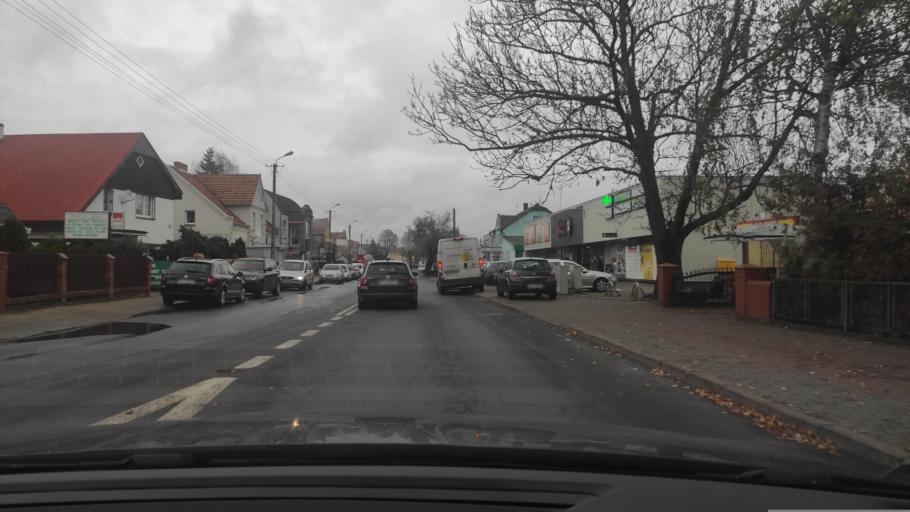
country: PL
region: Greater Poland Voivodeship
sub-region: Powiat poznanski
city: Kostrzyn
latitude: 52.3977
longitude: 17.2188
